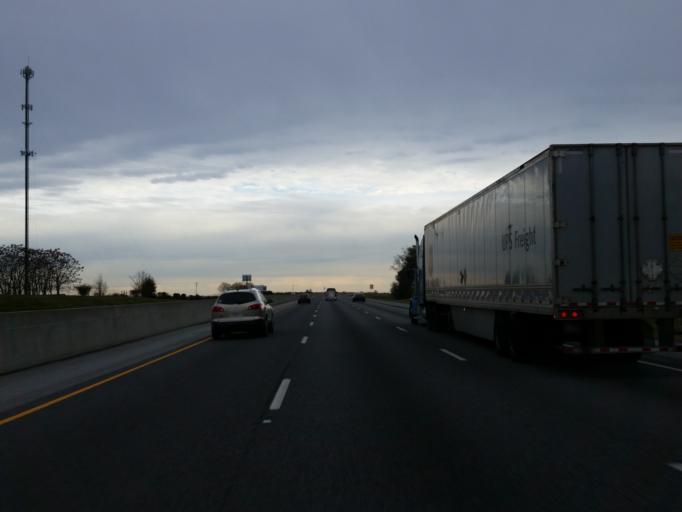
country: US
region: Georgia
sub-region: Turner County
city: Ashburn
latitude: 31.6200
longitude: -83.5712
